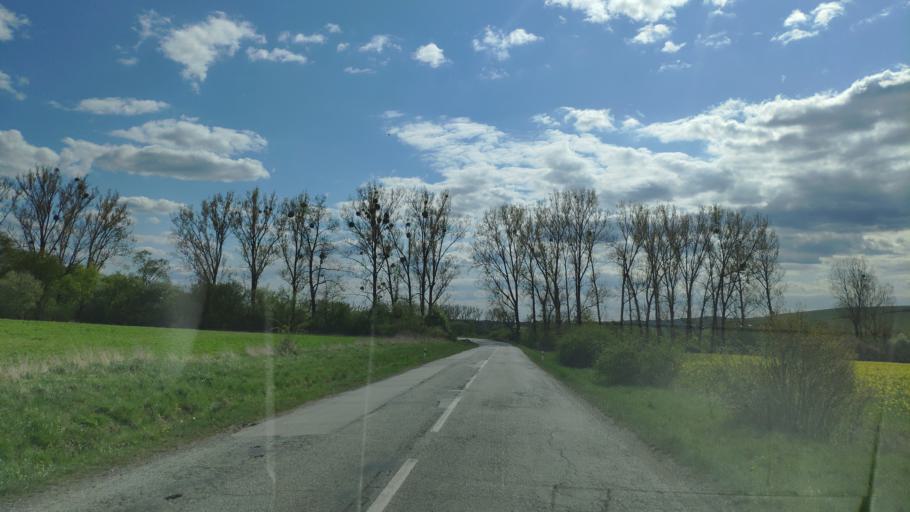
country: SK
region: Kosicky
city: Kosice
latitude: 48.6794
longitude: 21.4223
